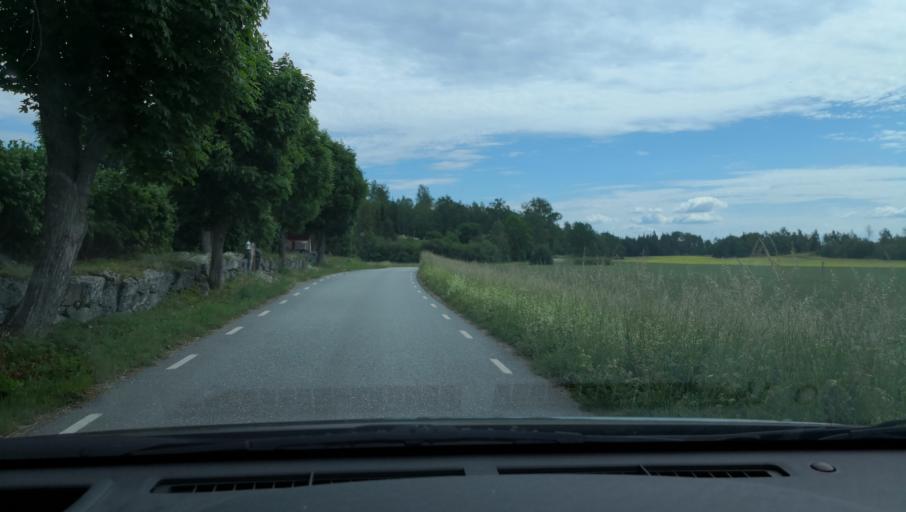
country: SE
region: Uppsala
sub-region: Enkopings Kommun
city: Orsundsbro
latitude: 59.7039
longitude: 17.4206
